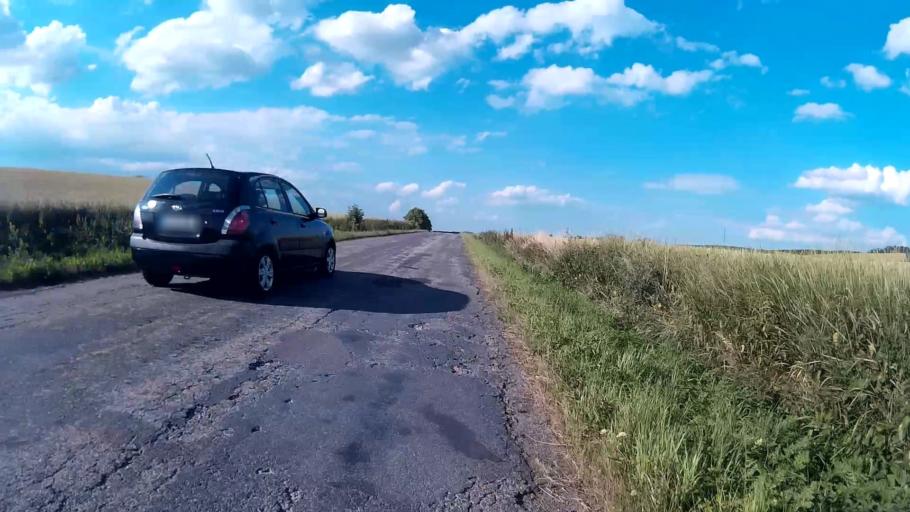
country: CZ
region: South Moravian
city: Tesany
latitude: 49.0576
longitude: 16.7798
